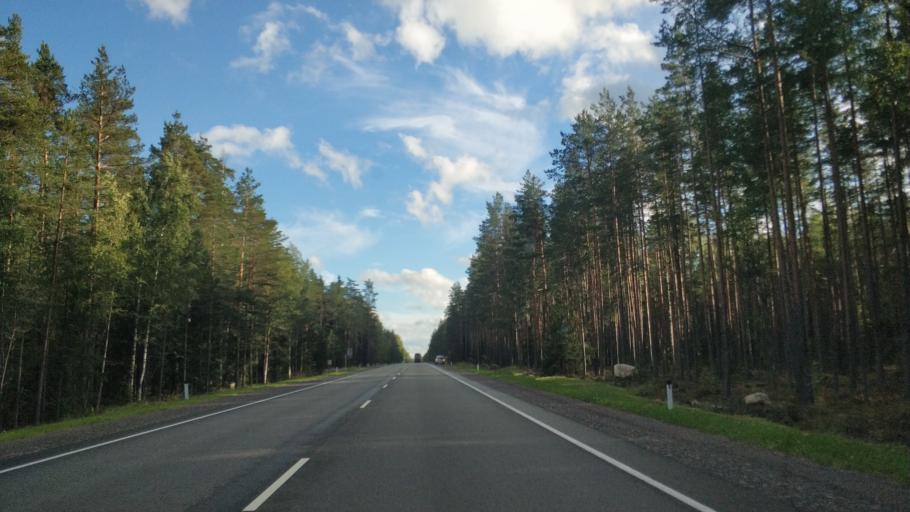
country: RU
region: Leningrad
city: Priozersk
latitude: 60.9036
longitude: 30.1602
